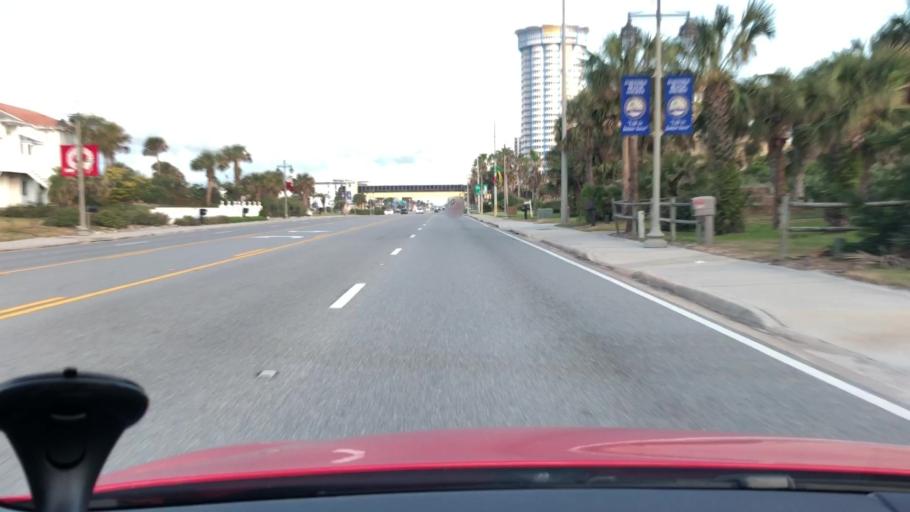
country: US
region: Florida
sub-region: Volusia County
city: Daytona Beach Shores
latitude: 29.1788
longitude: -80.9843
